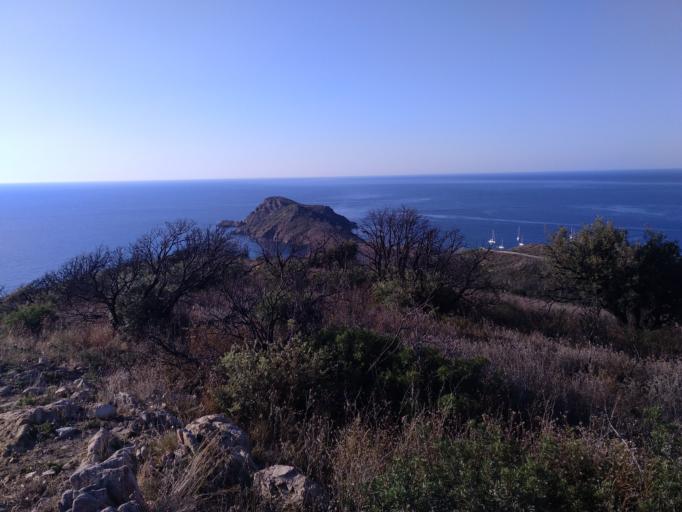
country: FR
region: Provence-Alpes-Cote d'Azur
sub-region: Departement du Var
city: Ramatuelle
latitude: 43.1787
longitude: 6.6372
